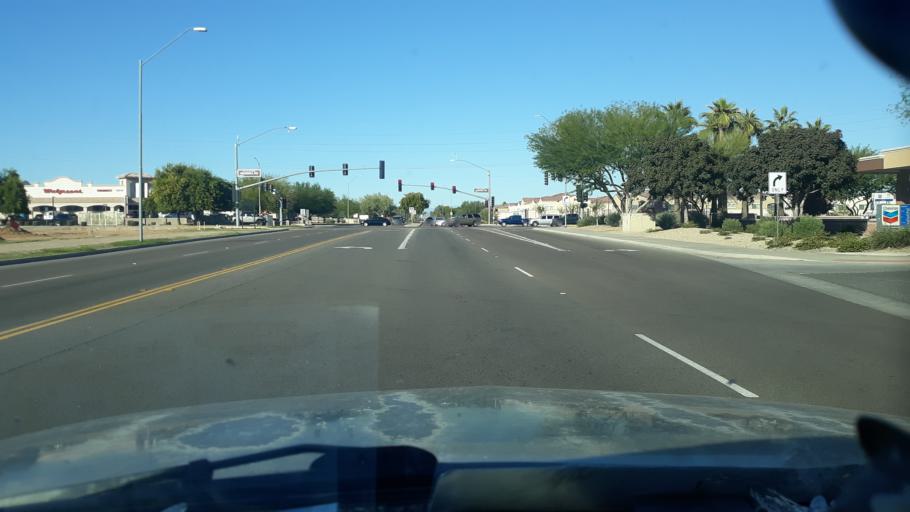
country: US
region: Arizona
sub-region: Maricopa County
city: Surprise
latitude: 33.6086
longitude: -112.3938
